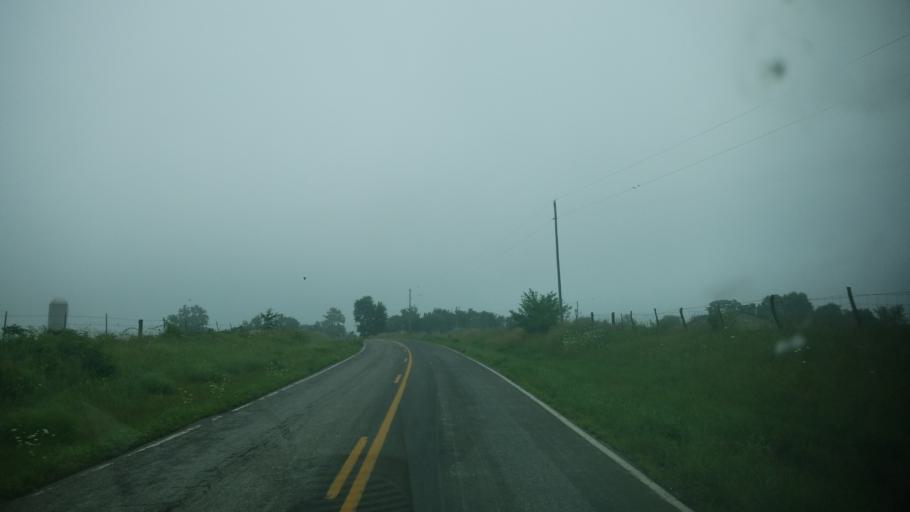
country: US
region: Missouri
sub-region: Audrain County
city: Vandalia
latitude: 39.2746
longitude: -91.3466
